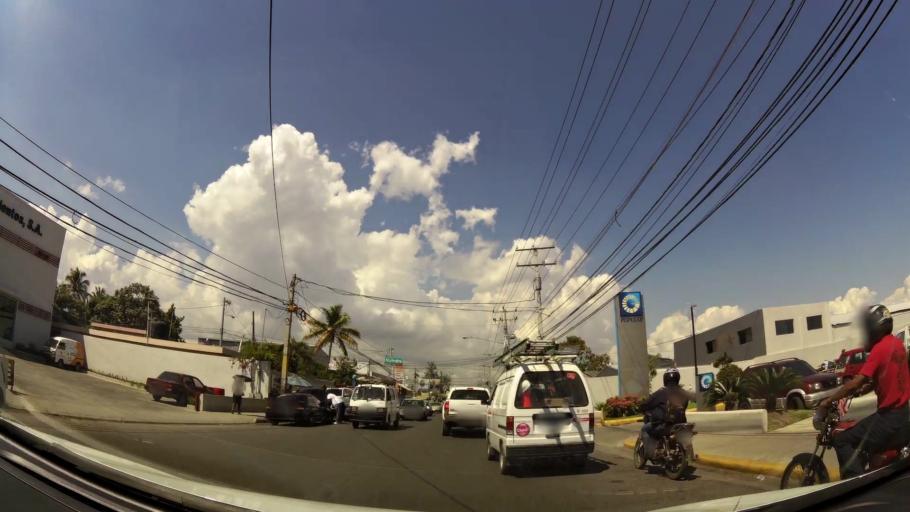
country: DO
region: Nacional
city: Bella Vista
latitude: 18.4565
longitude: -69.9775
